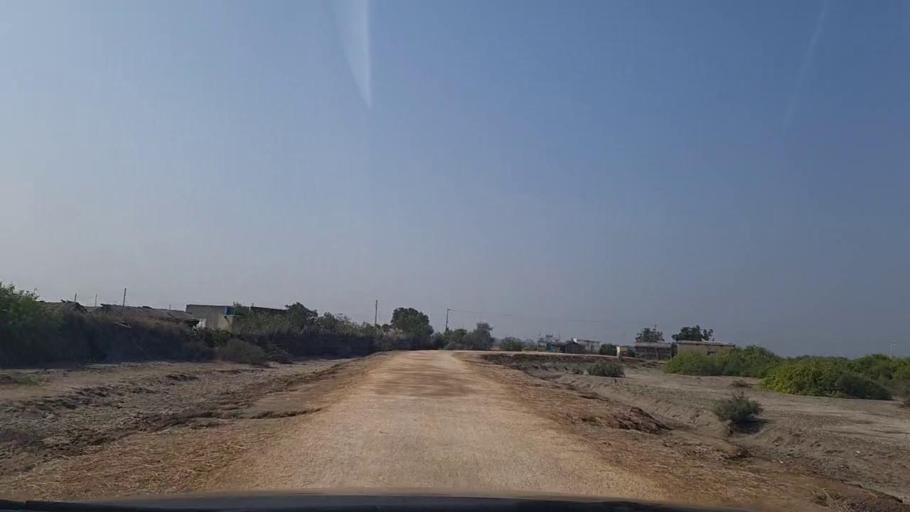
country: PK
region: Sindh
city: Mirpur Sakro
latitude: 24.5786
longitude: 67.7565
